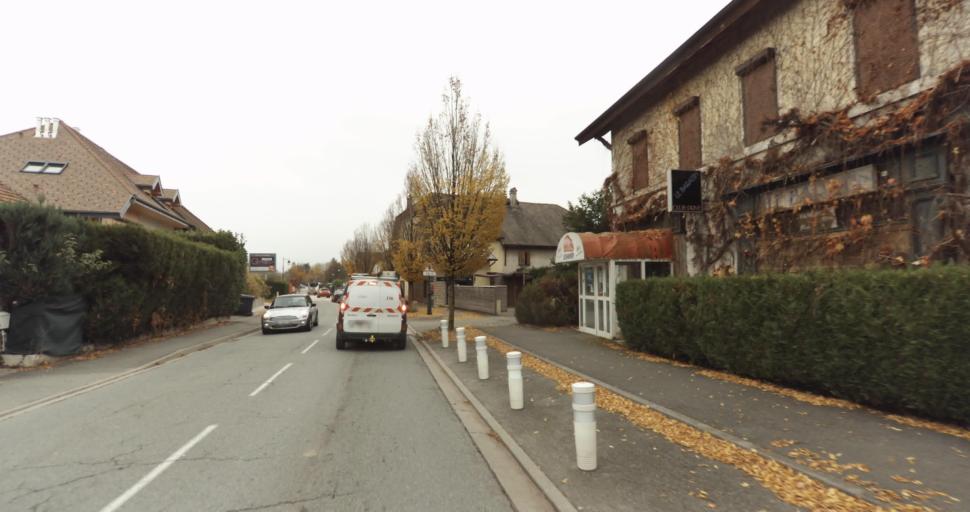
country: FR
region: Rhone-Alpes
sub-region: Departement de la Haute-Savoie
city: Epagny
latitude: 45.9278
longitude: 6.0843
